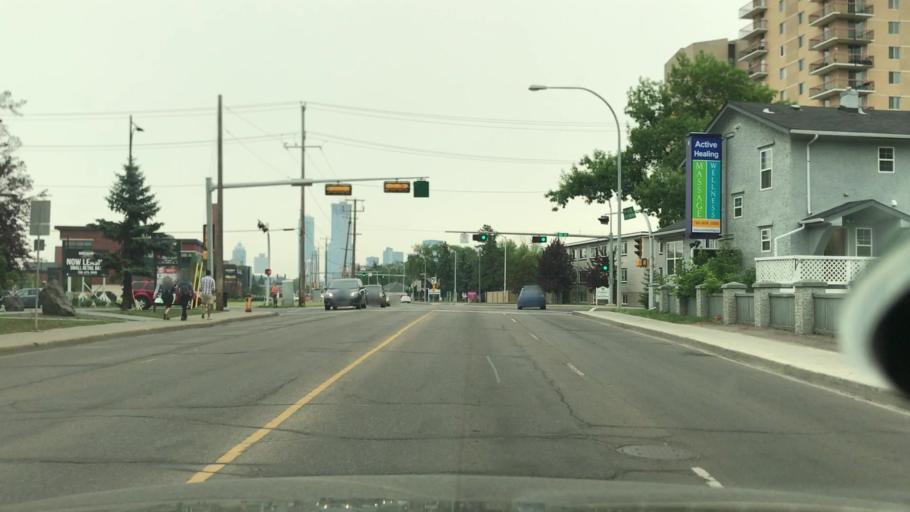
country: CA
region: Alberta
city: Edmonton
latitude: 53.5464
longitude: -113.5317
